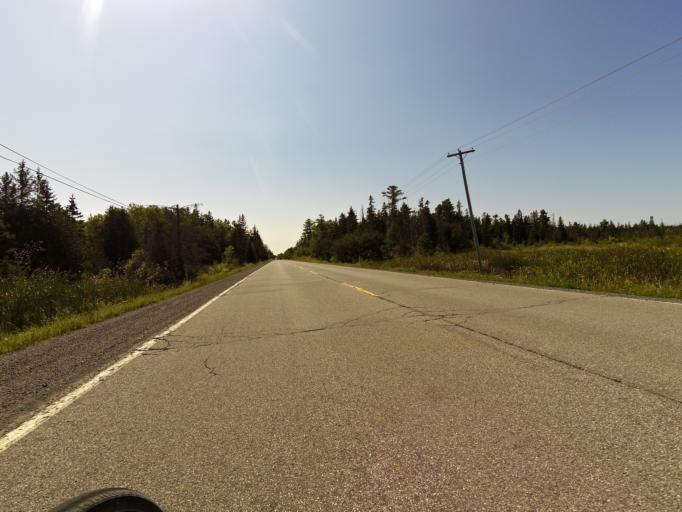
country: CA
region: Ontario
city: Bells Corners
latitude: 45.3928
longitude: -75.9321
